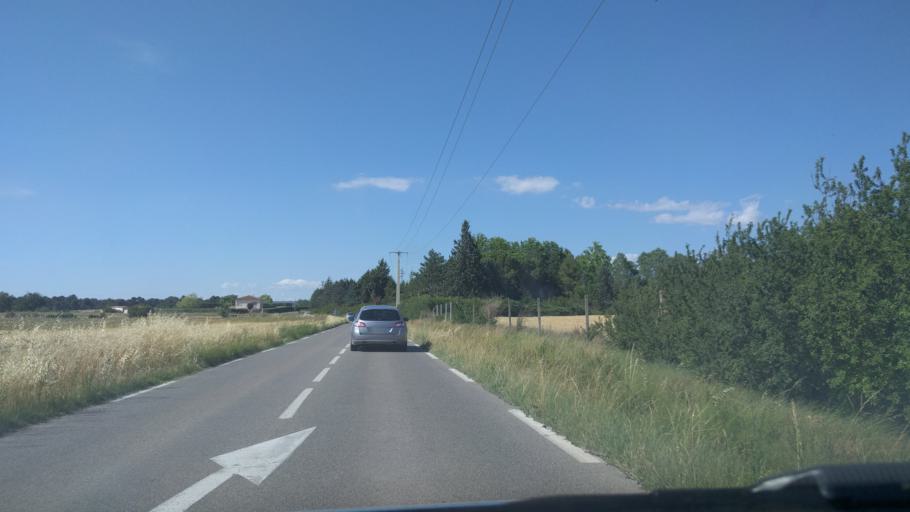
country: FR
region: Provence-Alpes-Cote d'Azur
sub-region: Departement des Bouches-du-Rhone
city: Eguilles
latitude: 43.5096
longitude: 5.3500
